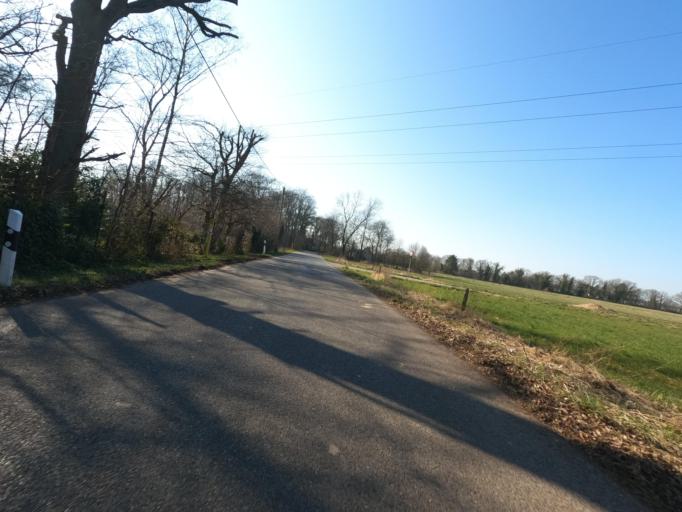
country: DE
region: North Rhine-Westphalia
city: Erkelenz
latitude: 51.0542
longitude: 6.3219
